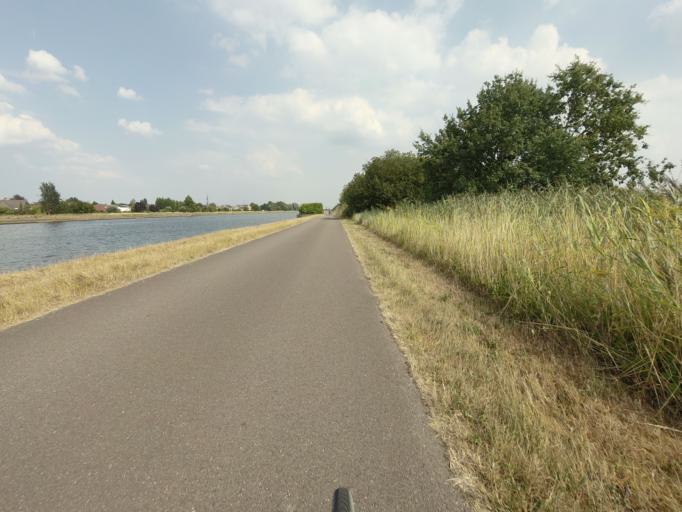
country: BE
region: Flanders
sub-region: Provincie Antwerpen
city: Ranst
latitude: 51.2116
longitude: 4.5842
